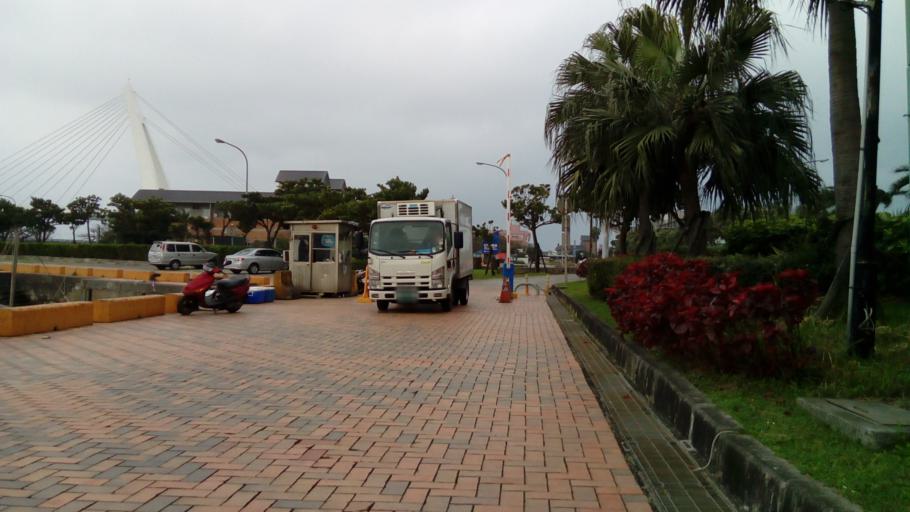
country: TW
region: Taipei
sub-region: Taipei
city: Banqiao
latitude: 25.1839
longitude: 121.4131
